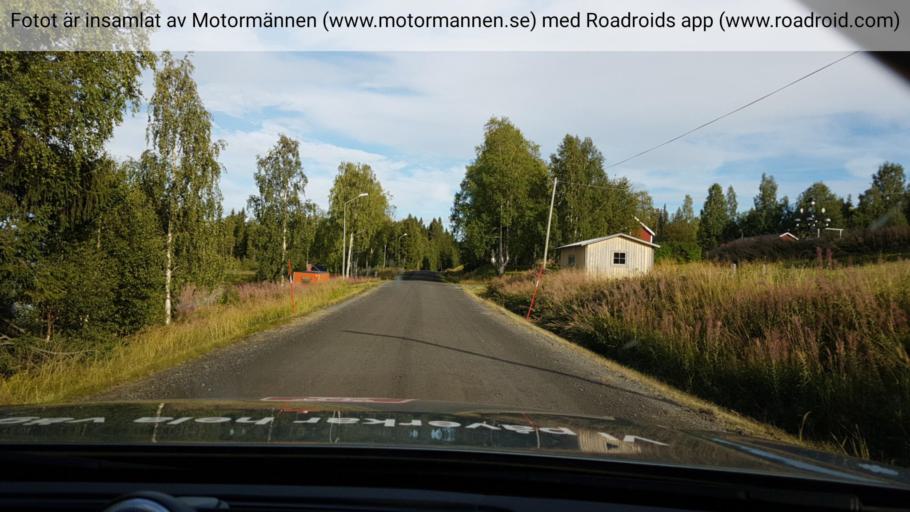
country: SE
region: Jaemtland
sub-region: Stroemsunds Kommun
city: Stroemsund
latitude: 64.1341
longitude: 15.7738
